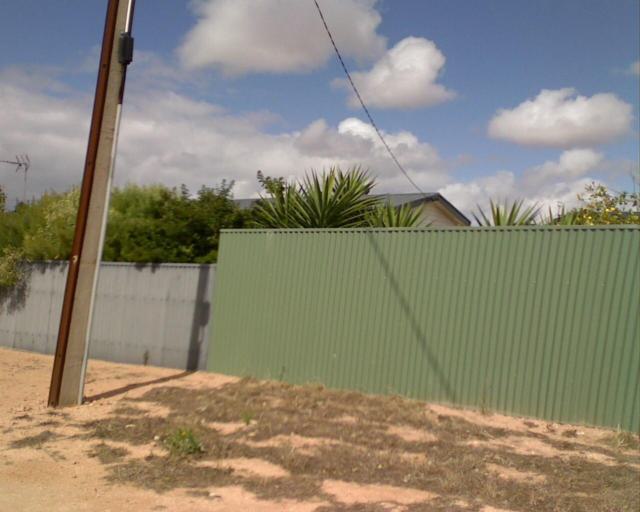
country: AU
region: South Australia
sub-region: Ceduna
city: Ceduna
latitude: -32.0999
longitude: 133.5771
